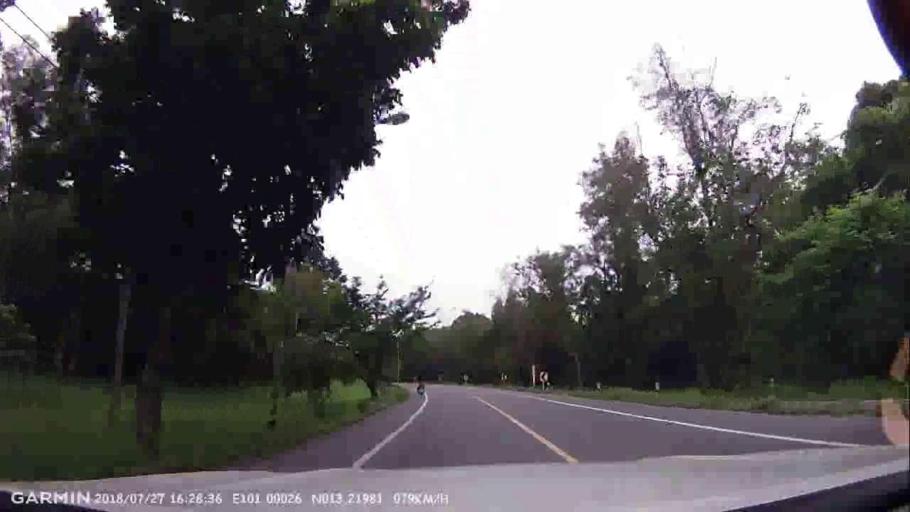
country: TH
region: Chon Buri
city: Si Racha
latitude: 13.2196
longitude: 101.0003
